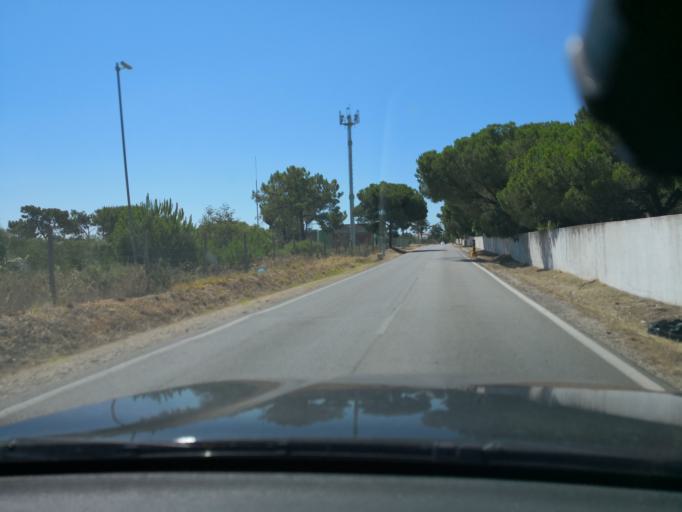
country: PT
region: Faro
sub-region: Loule
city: Vilamoura
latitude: 37.0821
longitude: -8.0998
